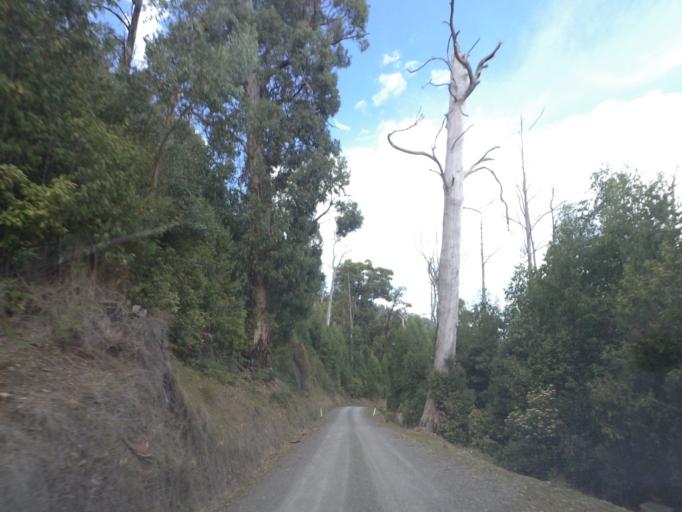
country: AU
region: Victoria
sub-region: Murrindindi
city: Alexandra
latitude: -37.4151
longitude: 145.7587
